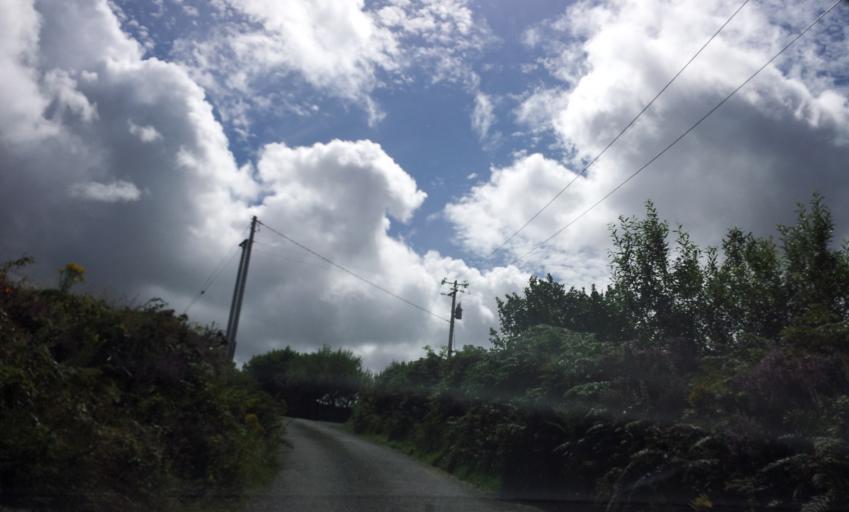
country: IE
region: Munster
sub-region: Ciarrai
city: Killorglin
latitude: 52.0467
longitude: -9.9876
